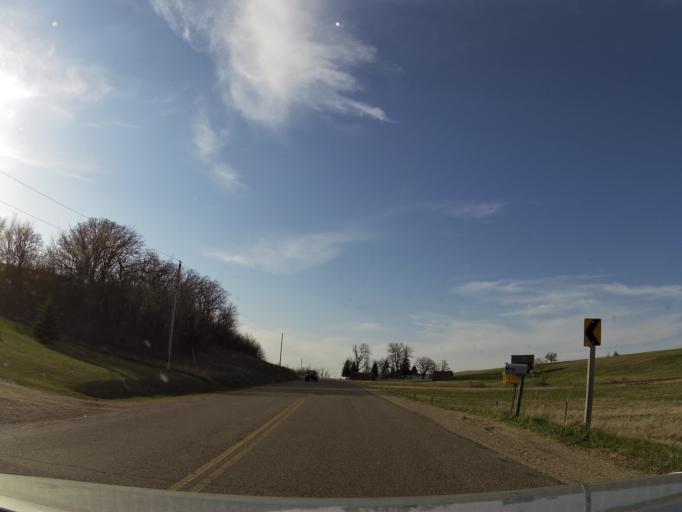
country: US
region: Wisconsin
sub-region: Pierce County
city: River Falls
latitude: 44.7834
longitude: -92.6407
